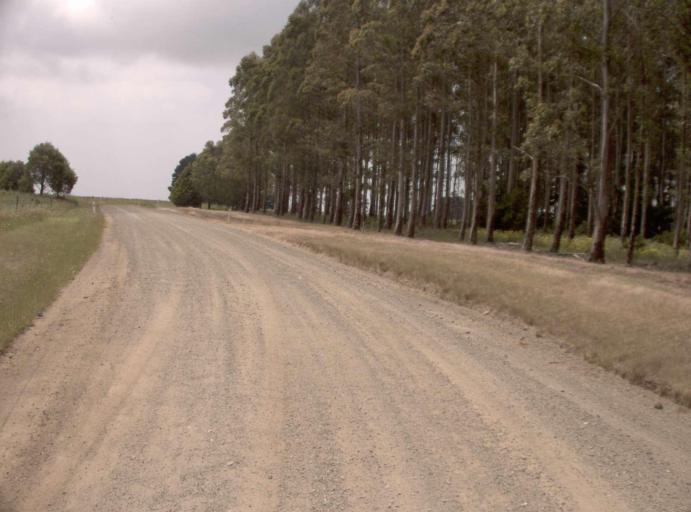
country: AU
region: Victoria
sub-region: Latrobe
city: Traralgon
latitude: -38.3770
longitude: 146.6753
